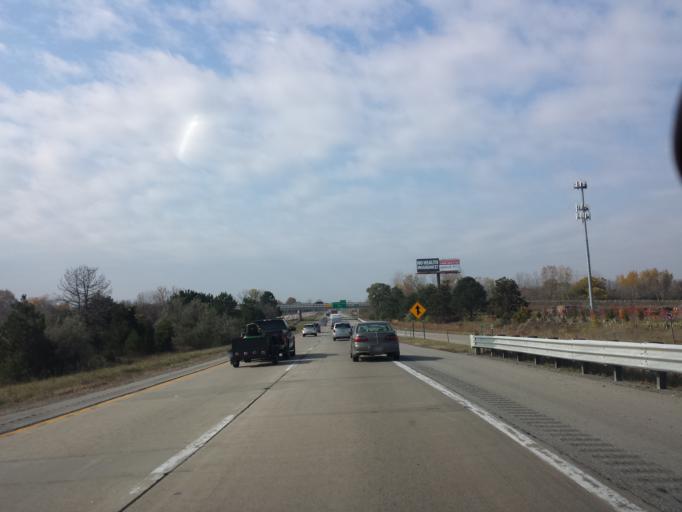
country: US
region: Michigan
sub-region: Saginaw County
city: Buena Vista
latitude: 43.4342
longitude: -83.8934
